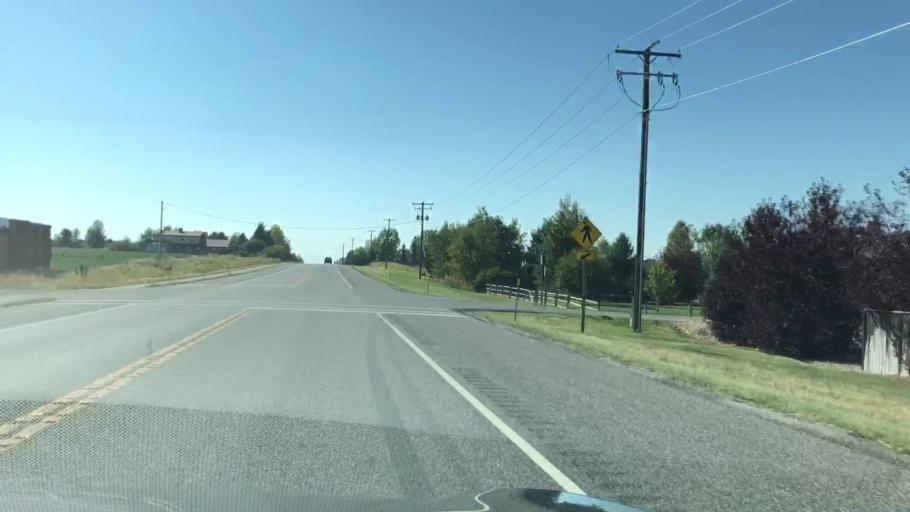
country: US
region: Montana
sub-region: Gallatin County
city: Belgrade
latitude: 45.7293
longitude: -111.1314
